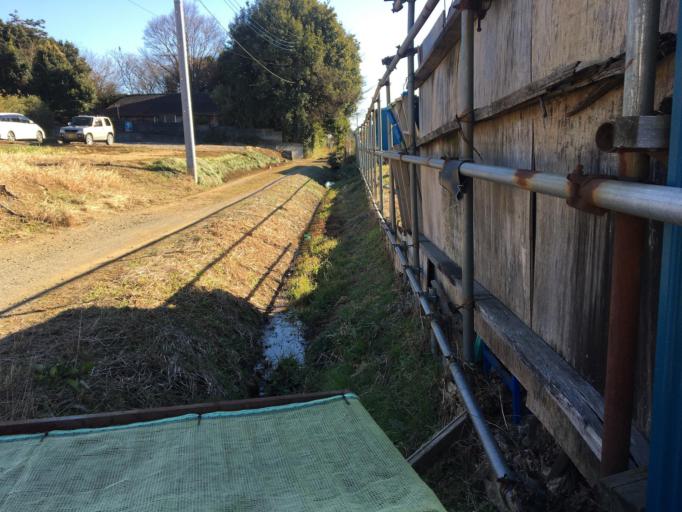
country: JP
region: Saitama
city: Ageoshimo
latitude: 35.9752
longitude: 139.6322
